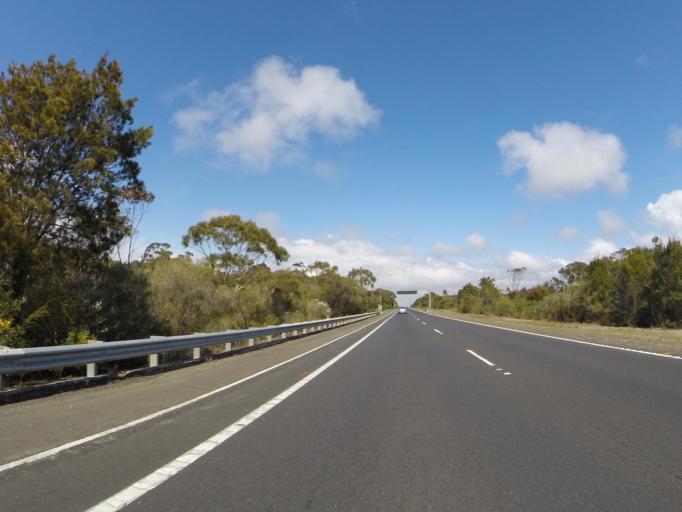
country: AU
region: New South Wales
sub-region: Wollongong
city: Bulli
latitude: -34.2533
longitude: 150.9336
